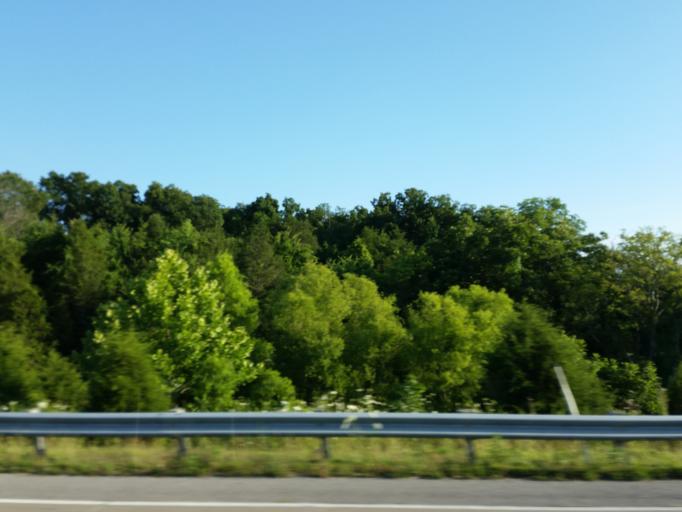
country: US
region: Tennessee
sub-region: Williamson County
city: Nolensville
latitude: 35.8452
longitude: -86.6533
